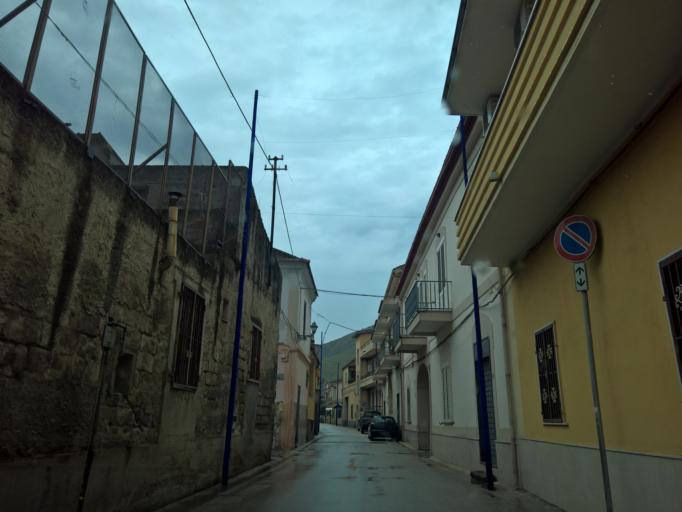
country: IT
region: Campania
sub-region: Provincia di Caserta
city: San Prisco
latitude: 41.0892
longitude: 14.2800
